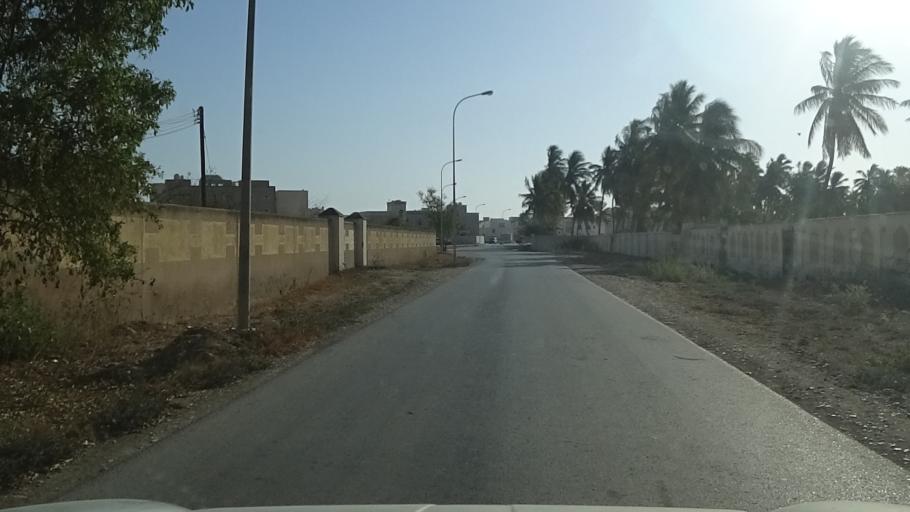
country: OM
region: Zufar
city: Salalah
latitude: 17.0206
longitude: 54.1532
